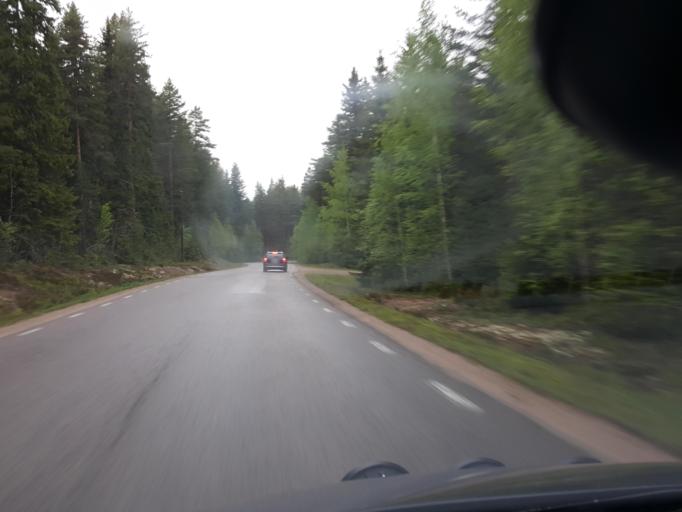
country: SE
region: Gaevleborg
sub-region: Ljusdals Kommun
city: Jaervsoe
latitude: 61.7817
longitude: 16.2166
